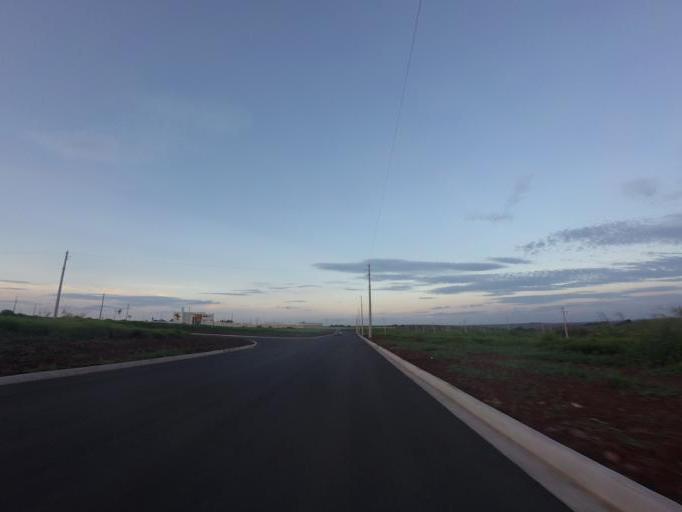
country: BR
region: Sao Paulo
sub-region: Piracicaba
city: Piracicaba
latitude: -22.7655
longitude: -47.5849
